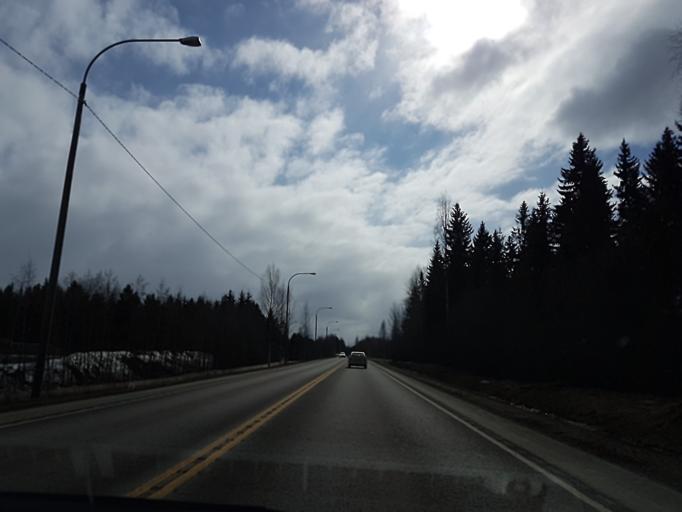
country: FI
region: Northern Savo
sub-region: Varkaus
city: Leppaevirta
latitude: 62.4754
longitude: 27.7724
